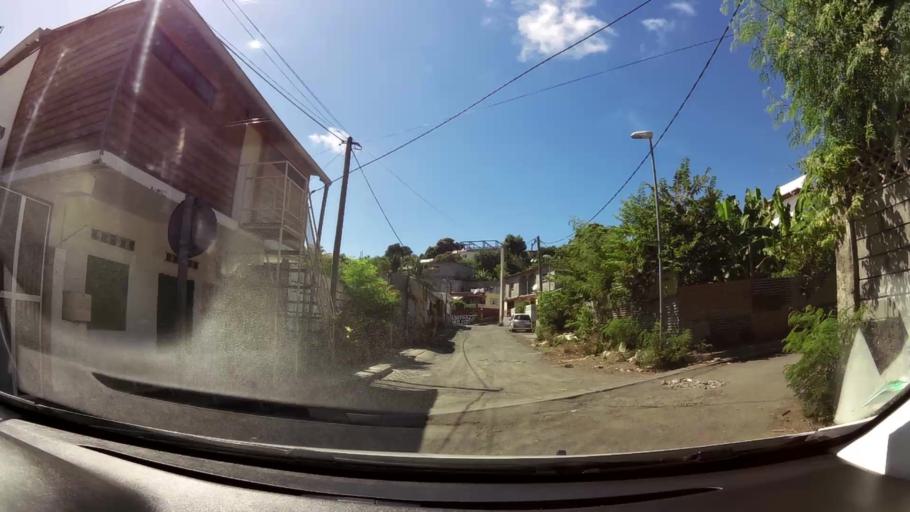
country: YT
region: Pamandzi
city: Pamandzi
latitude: -12.7994
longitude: 45.2803
